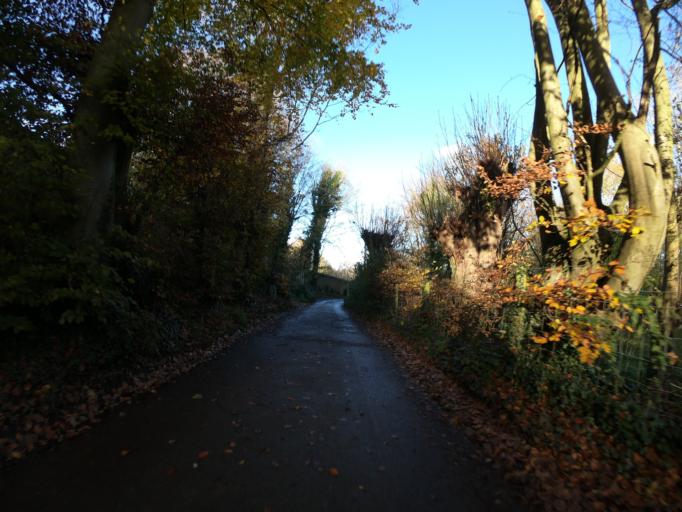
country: GB
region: England
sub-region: Kent
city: Eynsford
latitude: 51.3634
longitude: 0.1962
